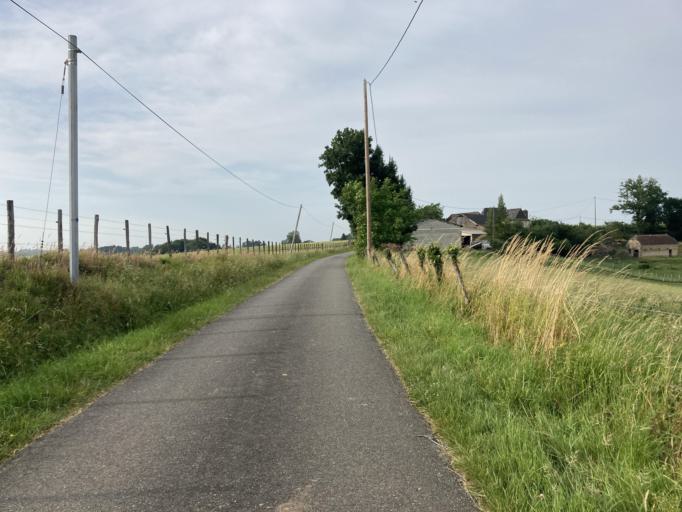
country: FR
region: Aquitaine
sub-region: Departement des Pyrenees-Atlantiques
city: Ledeuix
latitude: 43.2485
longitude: -0.6187
